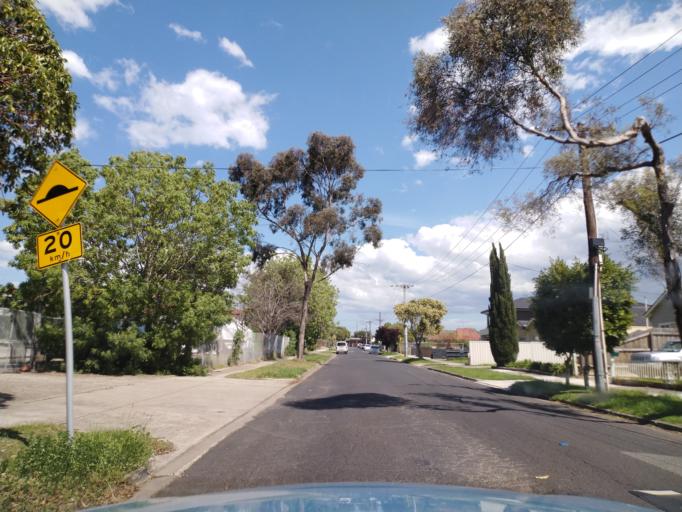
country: AU
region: Victoria
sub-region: Hobsons Bay
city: South Kingsville
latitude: -37.8317
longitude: 144.8745
